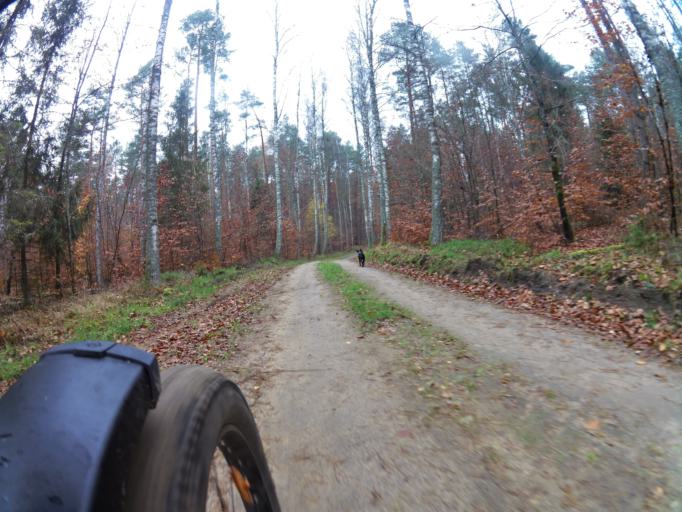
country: PL
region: Pomeranian Voivodeship
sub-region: Powiat wejherowski
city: Orle
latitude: 54.6940
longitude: 18.1562
